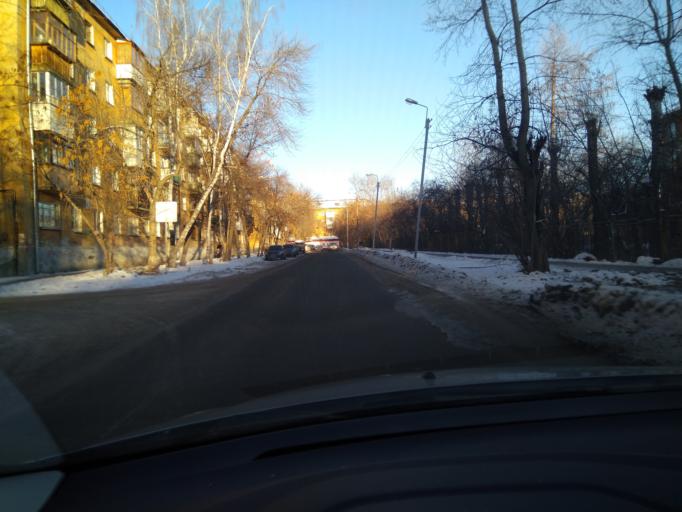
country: RU
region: Sverdlovsk
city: Yekaterinburg
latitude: 56.8879
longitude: 60.5712
